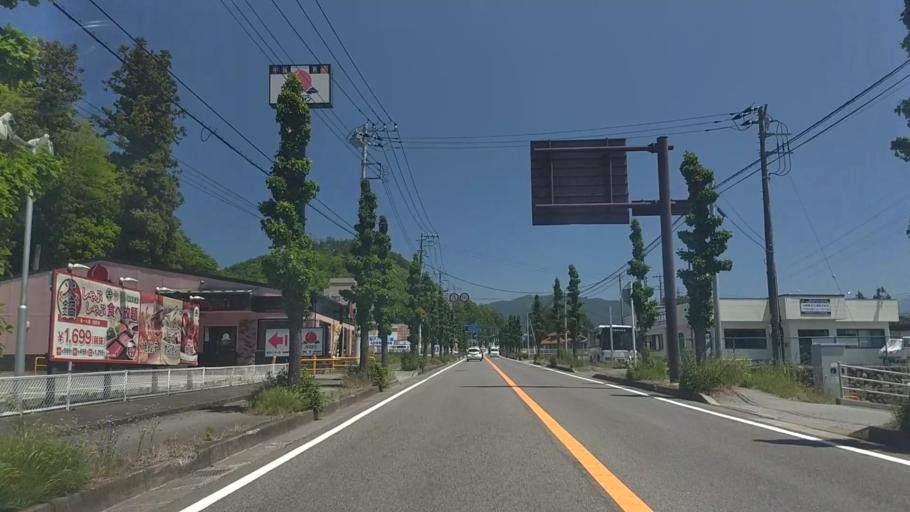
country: JP
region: Yamanashi
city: Nirasaki
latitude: 35.7917
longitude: 138.4195
